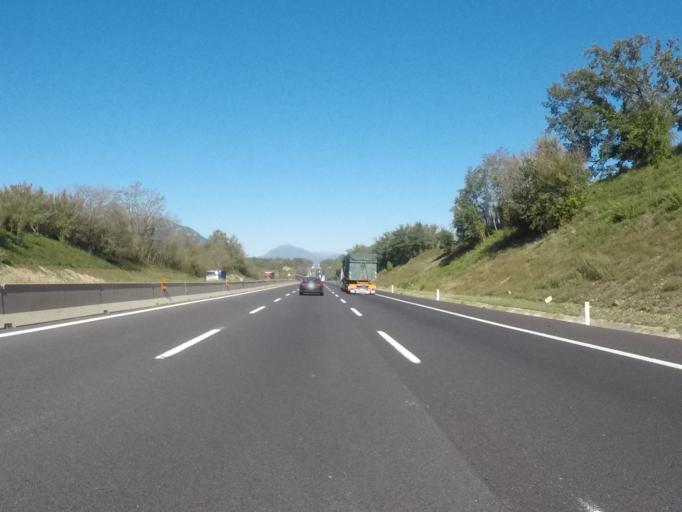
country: IT
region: Campania
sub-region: Provincia di Caserta
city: Tora
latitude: 41.3530
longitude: 14.0413
